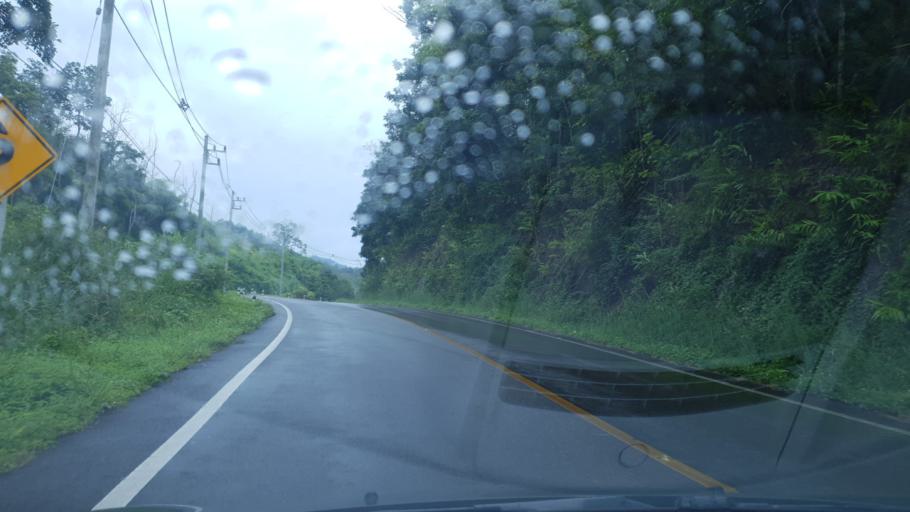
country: TH
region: Mae Hong Son
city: Mae La Noi
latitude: 18.6064
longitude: 97.9402
